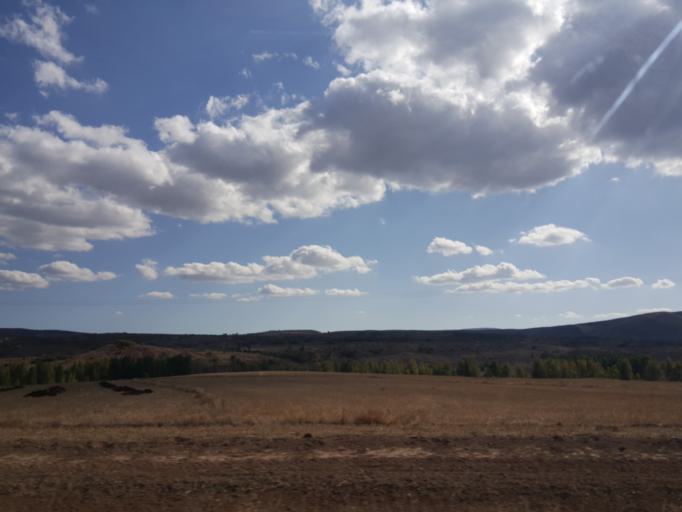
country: TR
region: Tokat
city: Sulusaray
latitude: 39.9751
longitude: 36.0309
